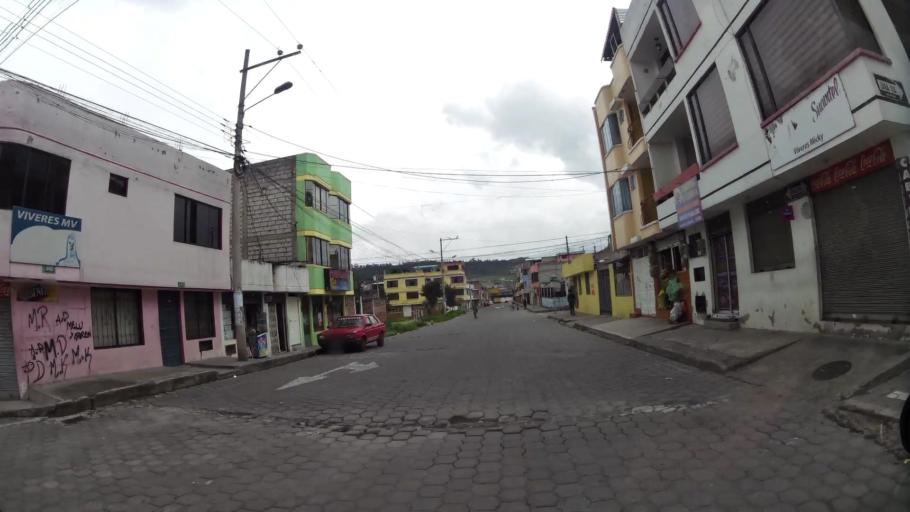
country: EC
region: Pichincha
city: Quito
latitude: -0.3124
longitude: -78.5463
